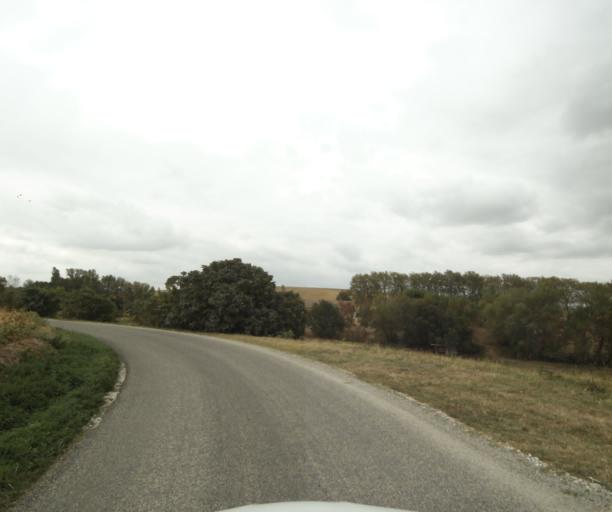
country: FR
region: Midi-Pyrenees
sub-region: Departement de la Haute-Garonne
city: Villefranche-de-Lauragais
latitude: 43.4034
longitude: 1.7336
